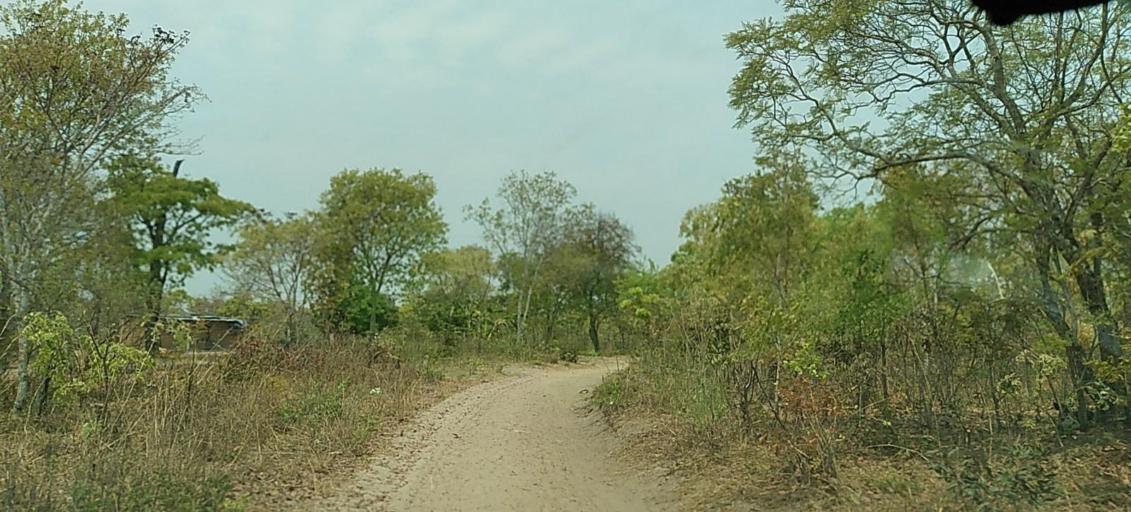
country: ZM
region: North-Western
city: Kabompo
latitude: -13.5374
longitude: 24.4561
